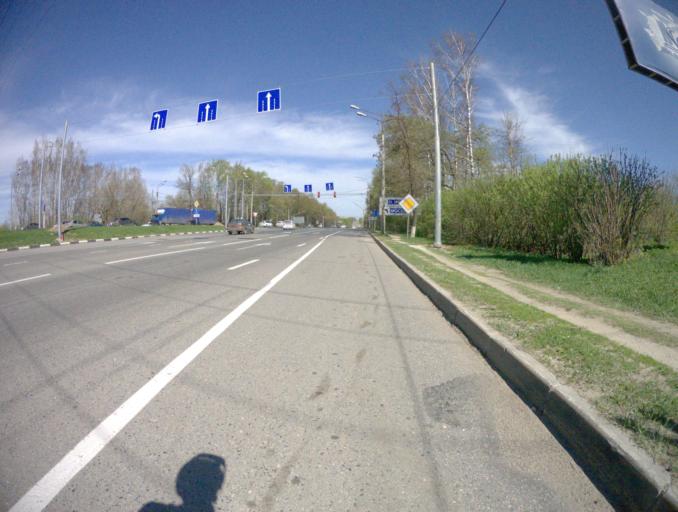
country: RU
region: Vladimir
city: Bogolyubovo
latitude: 56.1759
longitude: 40.4991
